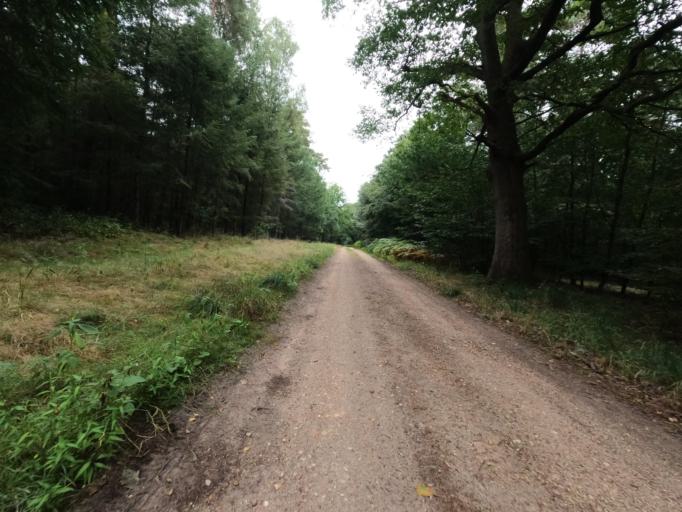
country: DE
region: North Rhine-Westphalia
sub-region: Regierungsbezirk Dusseldorf
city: Niederkruchten
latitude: 51.1759
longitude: 6.1726
